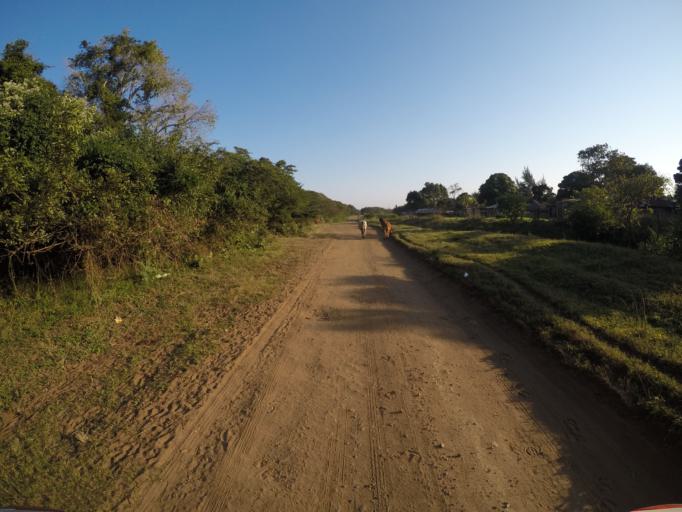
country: ZA
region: KwaZulu-Natal
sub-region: uThungulu District Municipality
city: KwaMbonambi
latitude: -28.6984
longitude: 32.1941
